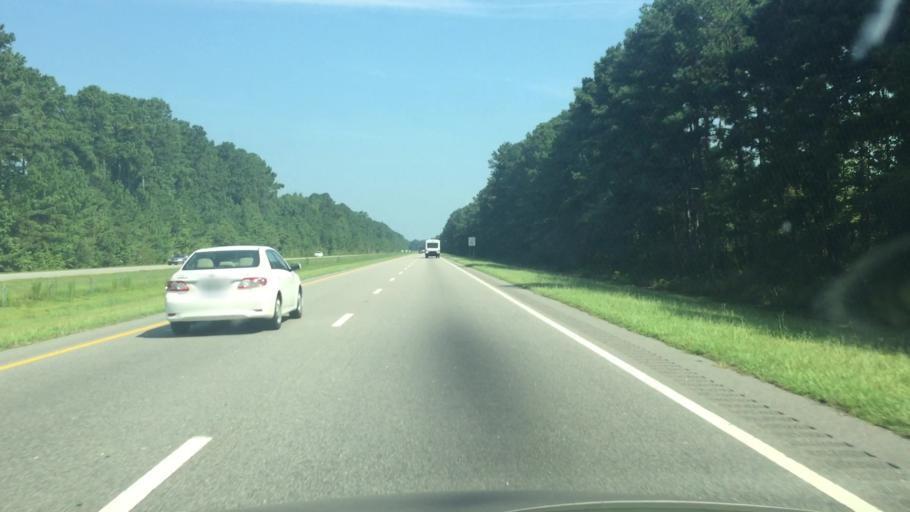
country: US
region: North Carolina
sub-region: Robeson County
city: Lumberton
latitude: 34.5475
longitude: -79.0224
